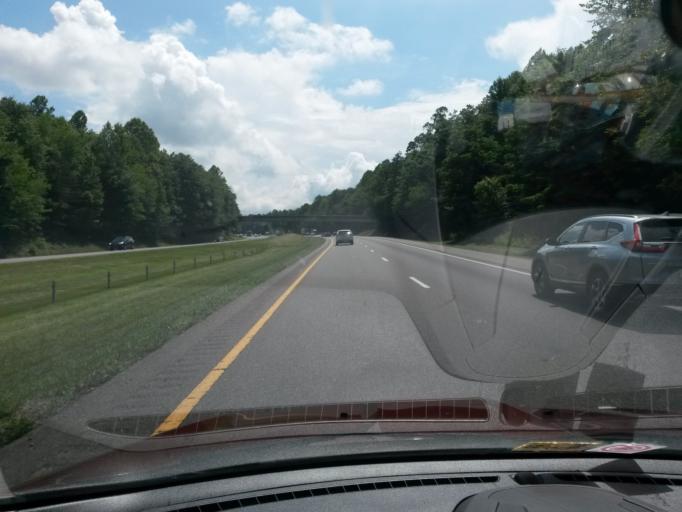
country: US
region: North Carolina
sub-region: Surry County
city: Dobson
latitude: 36.4619
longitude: -80.7649
